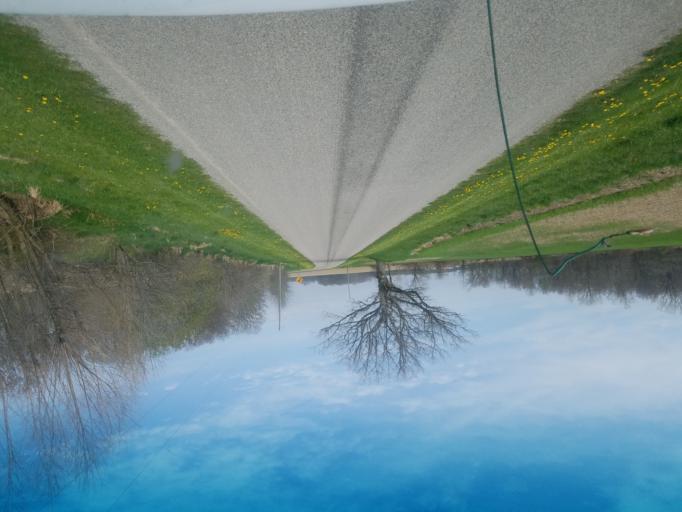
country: US
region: Ohio
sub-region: Union County
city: Richwood
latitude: 40.4838
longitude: -83.4580
